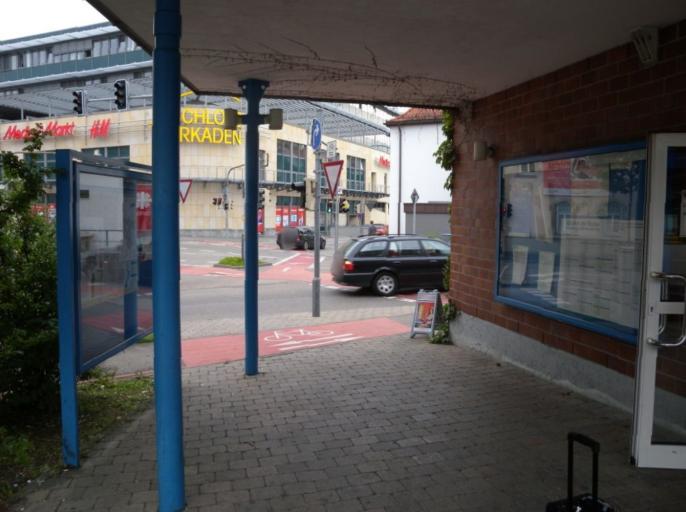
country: DE
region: Baden-Wuerttemberg
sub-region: Regierungsbezirk Stuttgart
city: Heidenheim an der Brenz
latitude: 48.6808
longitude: 10.1545
